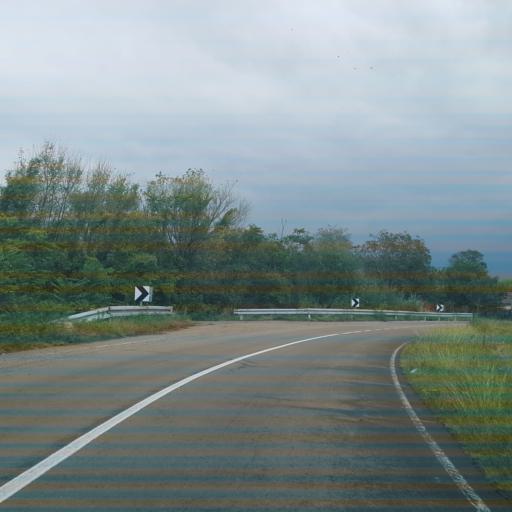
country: RS
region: Central Serbia
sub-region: Nisavski Okrug
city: Razanj
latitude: 43.6209
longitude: 21.5780
